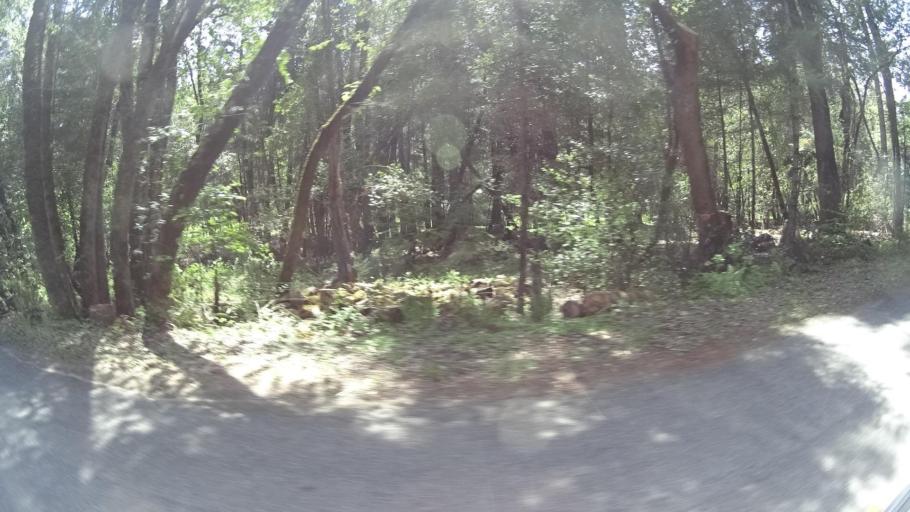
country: US
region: California
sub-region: Humboldt County
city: Redway
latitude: 40.3577
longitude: -123.7233
